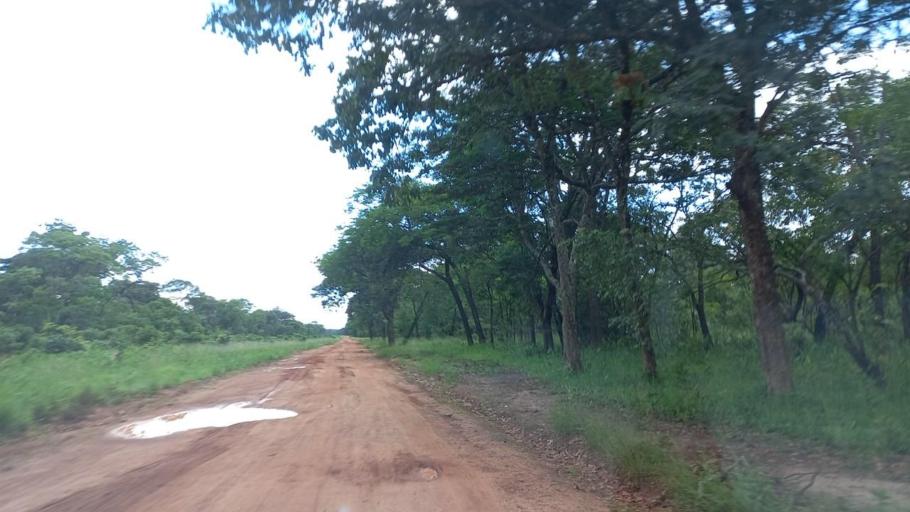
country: ZM
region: North-Western
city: Mwinilunga
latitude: -11.8013
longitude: 24.3701
